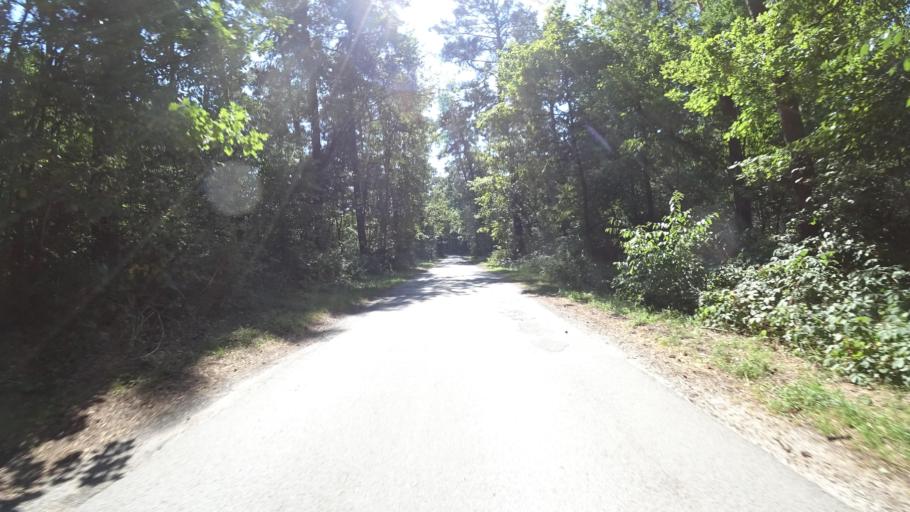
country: DE
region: North Rhine-Westphalia
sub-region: Regierungsbezirk Detmold
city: Steinhagen
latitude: 51.9501
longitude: 8.4583
